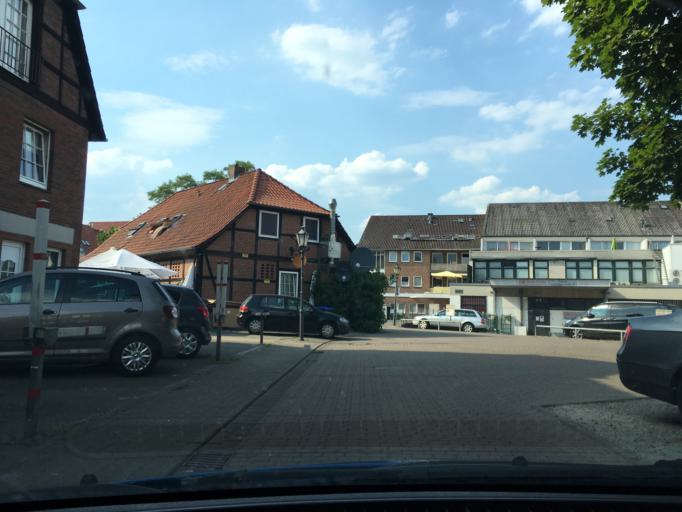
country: DE
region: Lower Saxony
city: Bad Bevensen
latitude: 53.0794
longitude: 10.5792
